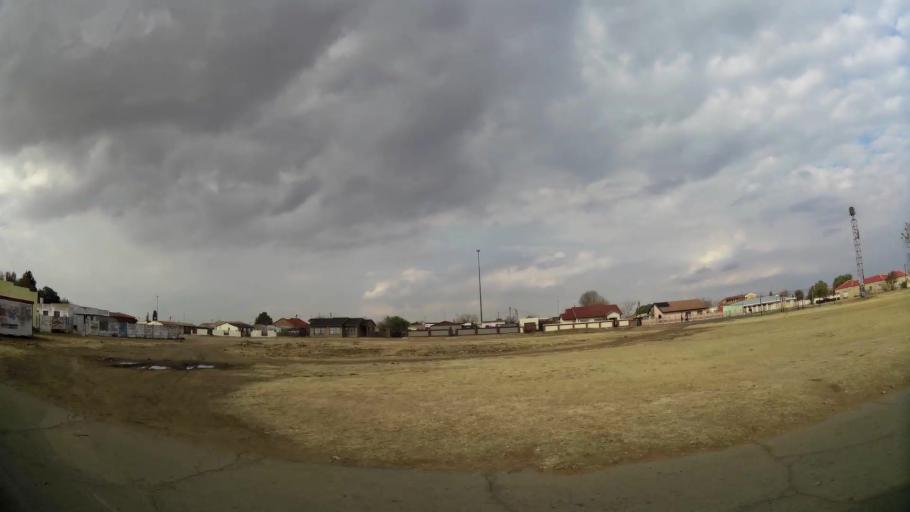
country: ZA
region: Orange Free State
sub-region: Fezile Dabi District Municipality
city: Sasolburg
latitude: -26.8401
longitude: 27.8477
